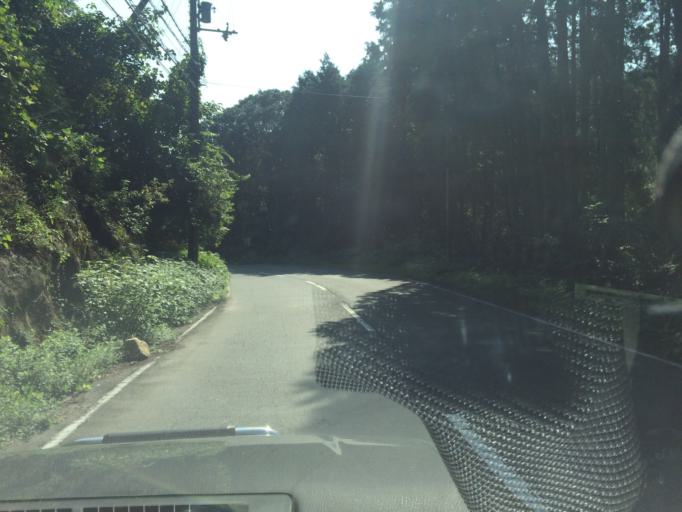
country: JP
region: Mie
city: Ueno-ebisumachi
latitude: 34.7332
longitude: 135.9785
